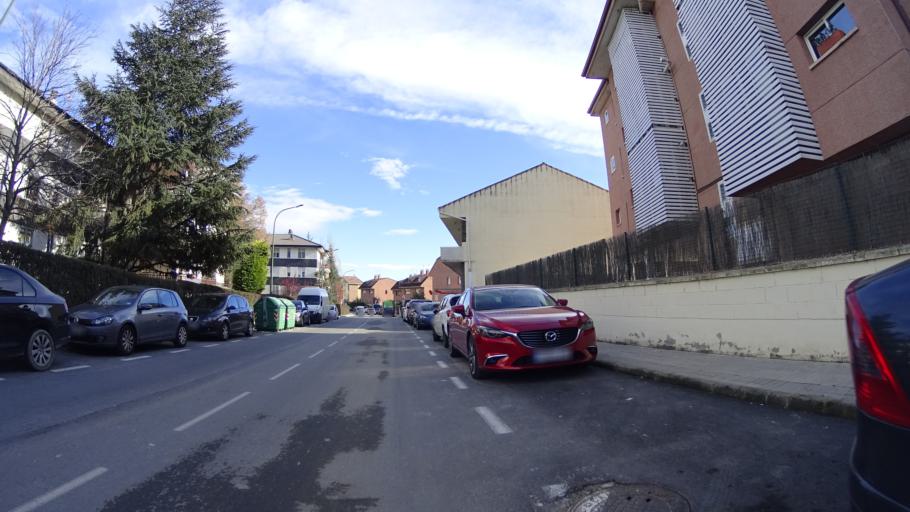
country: ES
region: Madrid
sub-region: Provincia de Madrid
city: Galapagar
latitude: 40.5800
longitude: -4.0144
